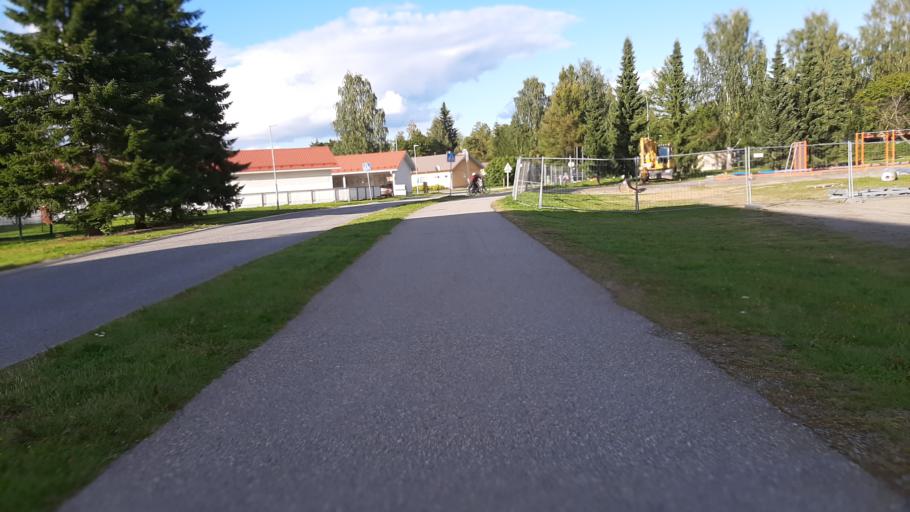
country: FI
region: North Karelia
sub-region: Joensuu
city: Joensuu
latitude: 62.6132
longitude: 29.7885
